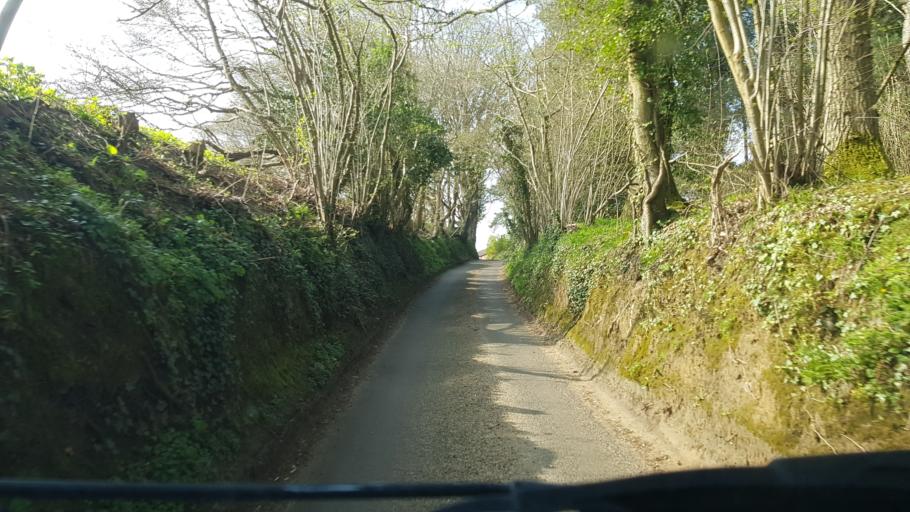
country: GB
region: England
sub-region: Surrey
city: Chilworth
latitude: 51.2242
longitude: -0.5113
